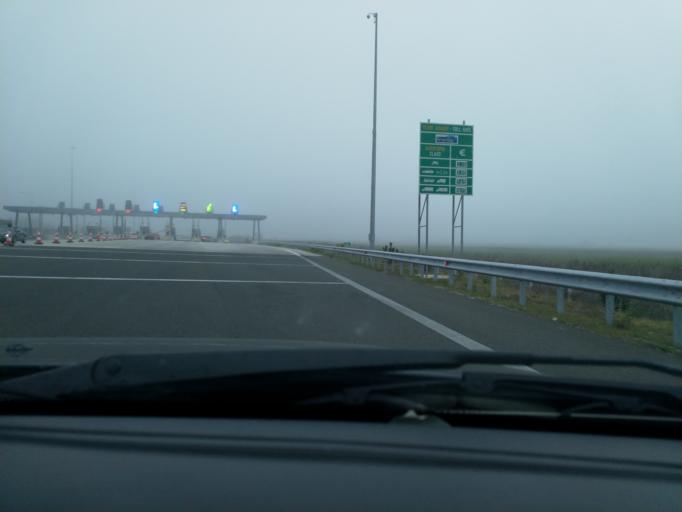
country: GR
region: Thessaly
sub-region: Nomos Kardhitsas
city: Anavra
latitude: 39.2558
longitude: 22.0829
